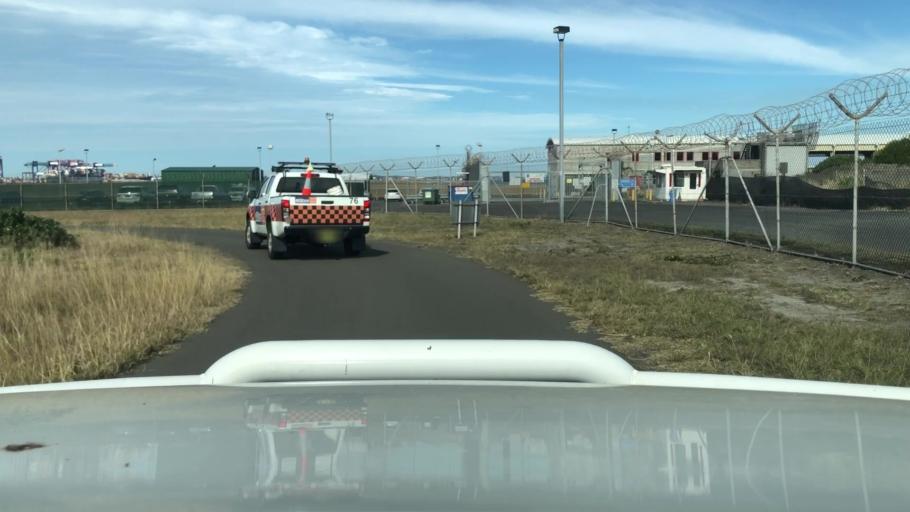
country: AU
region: New South Wales
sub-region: Botany Bay
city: Botany
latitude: -33.9478
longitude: 151.1855
